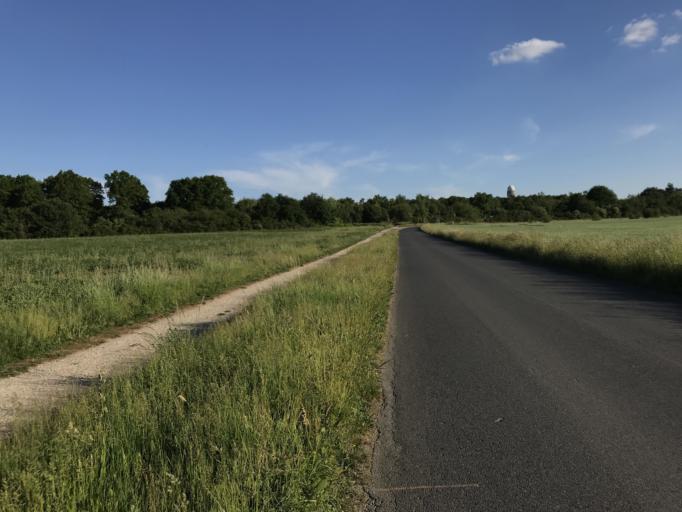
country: FR
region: Ile-de-France
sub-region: Departement de l'Essonne
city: Igny
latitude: 48.7229
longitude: 2.2231
